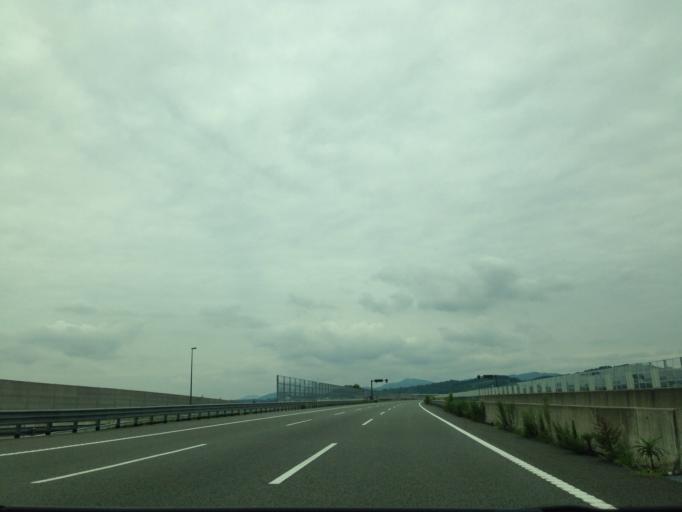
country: JP
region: Shizuoka
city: Hamakita
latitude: 34.8339
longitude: 137.8175
